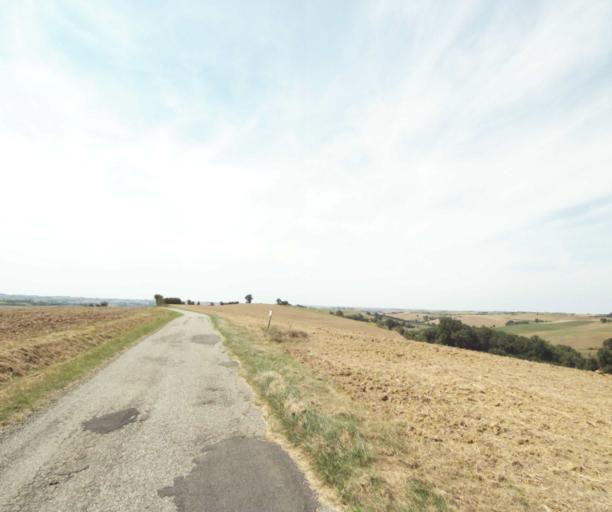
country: FR
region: Midi-Pyrenees
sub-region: Departement de la Haute-Garonne
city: Gaillac-Toulza
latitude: 43.2479
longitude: 1.4127
